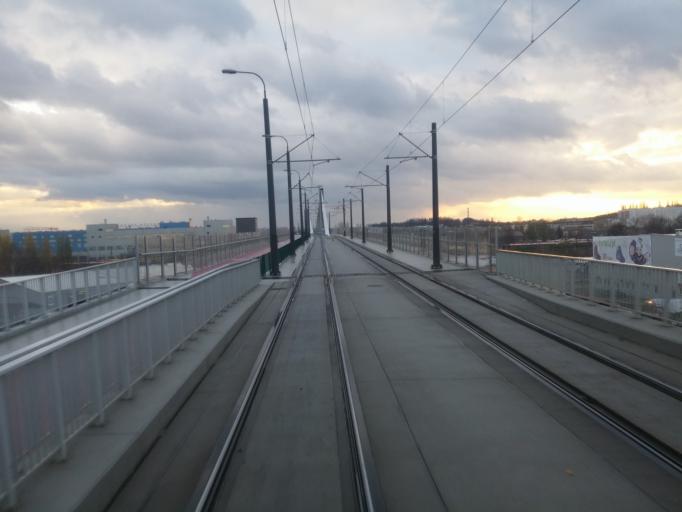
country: PL
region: Lesser Poland Voivodeship
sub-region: Krakow
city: Krakow
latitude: 50.0358
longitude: 19.9810
